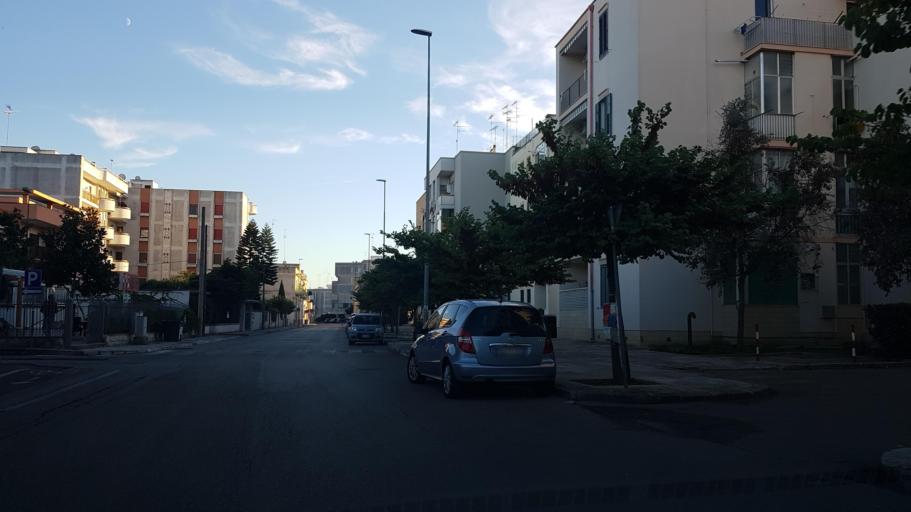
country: IT
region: Apulia
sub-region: Provincia di Lecce
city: Lecce
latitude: 40.3651
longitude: 18.1768
